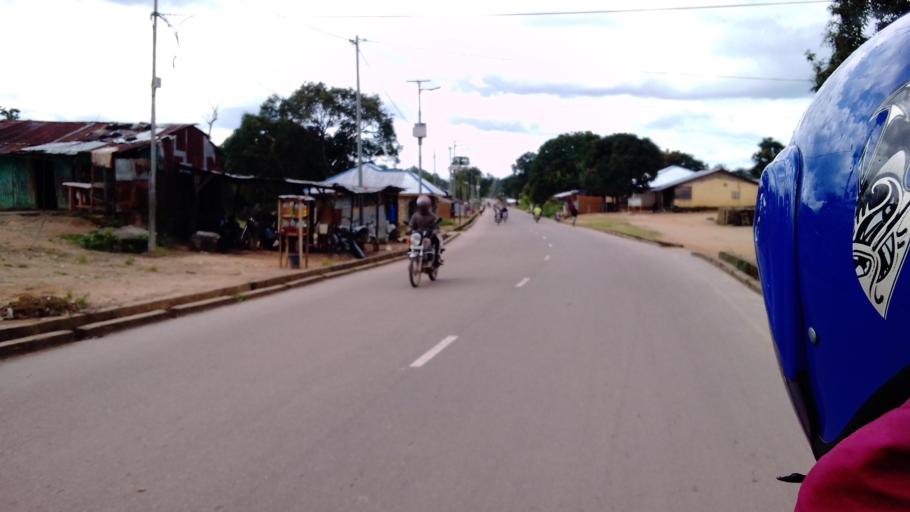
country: SL
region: Eastern Province
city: Koidu
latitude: 8.6520
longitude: -10.9753
